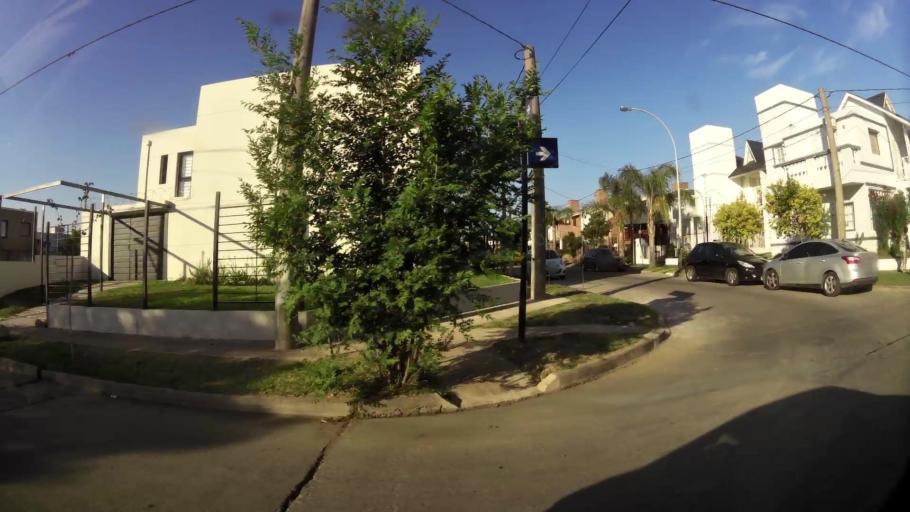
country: AR
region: Cordoba
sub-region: Departamento de Capital
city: Cordoba
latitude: -31.3846
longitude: -64.2447
